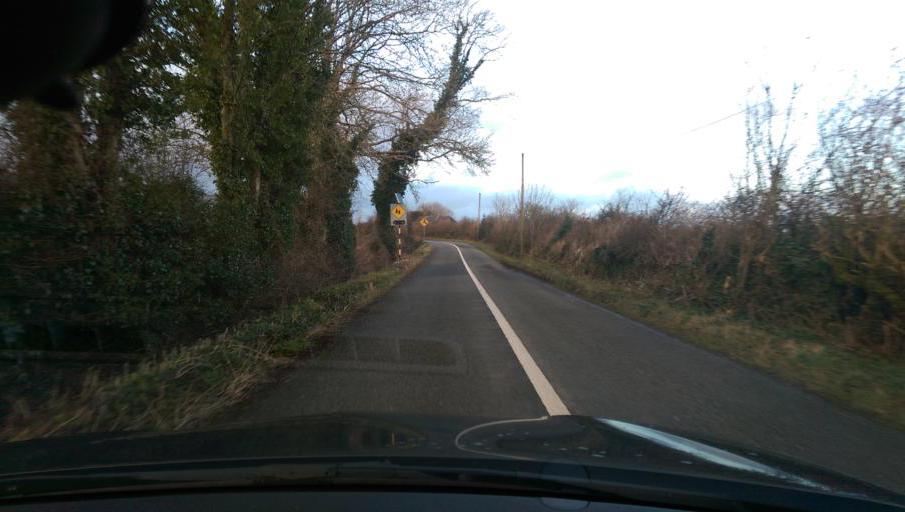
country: IE
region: Connaught
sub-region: County Galway
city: Ballinasloe
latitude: 53.4604
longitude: -8.3749
